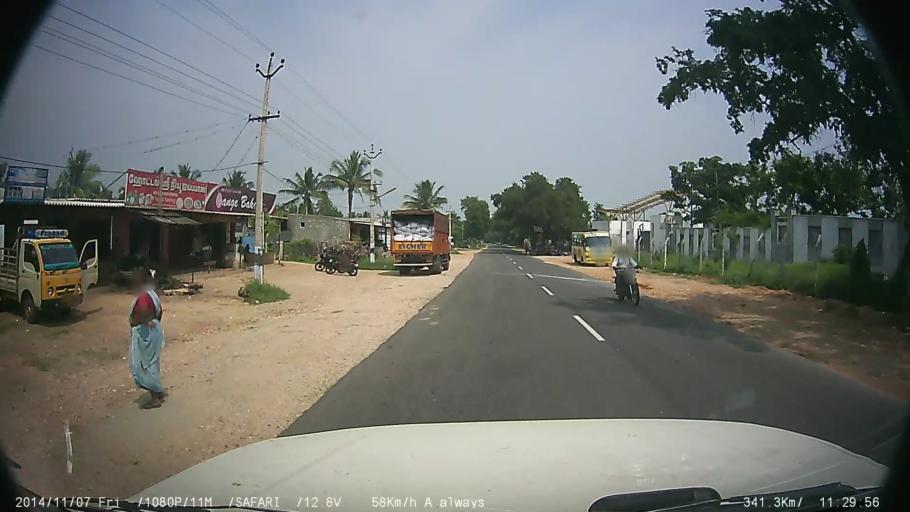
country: IN
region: Tamil Nadu
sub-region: Tiruppur
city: Avinashi
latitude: 11.1587
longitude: 77.2671
